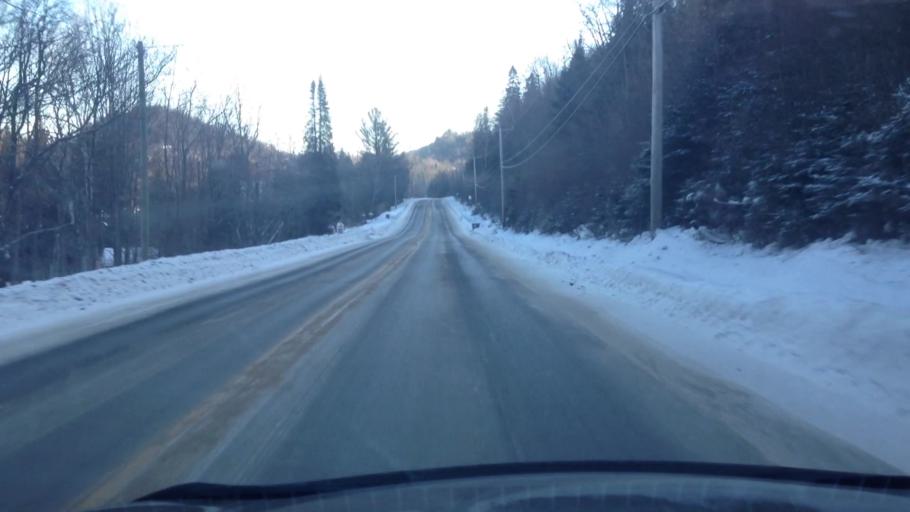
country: CA
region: Quebec
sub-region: Laurentides
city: Sainte-Agathe-des-Monts
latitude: 45.9153
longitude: -74.3688
